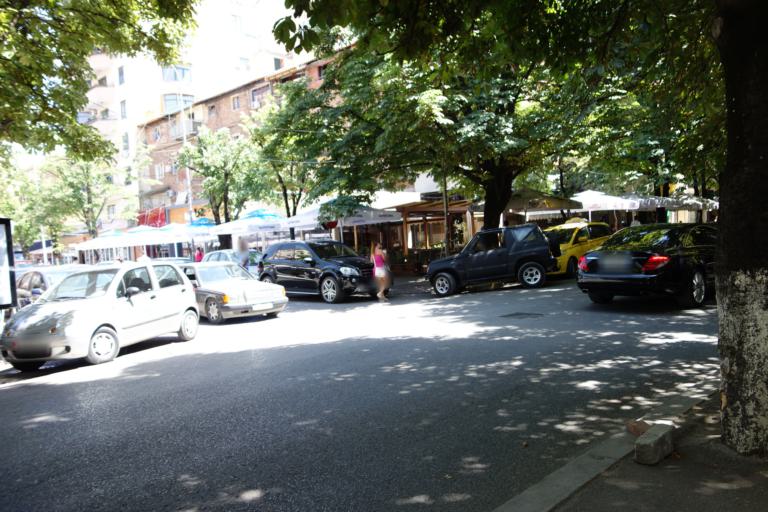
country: AL
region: Tirane
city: Tirana
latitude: 41.3203
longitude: 19.8139
